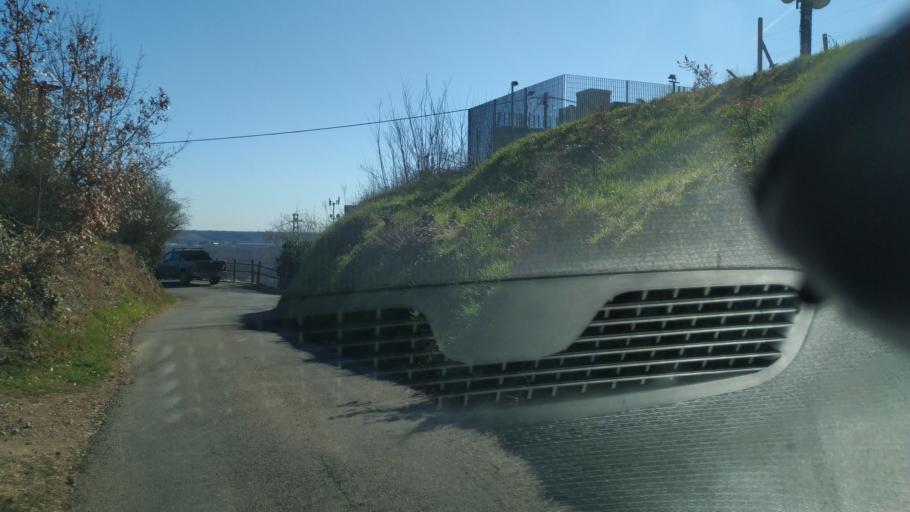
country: IT
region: Piedmont
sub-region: Provincia di Vercelli
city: Gattinara
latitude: 45.6224
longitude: 8.3658
